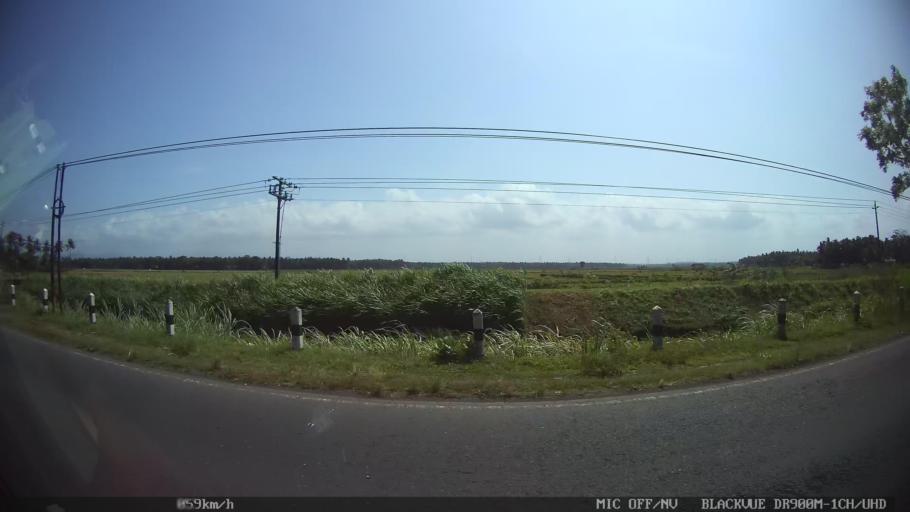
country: ID
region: Daerah Istimewa Yogyakarta
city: Srandakan
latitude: -7.9407
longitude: 110.1619
